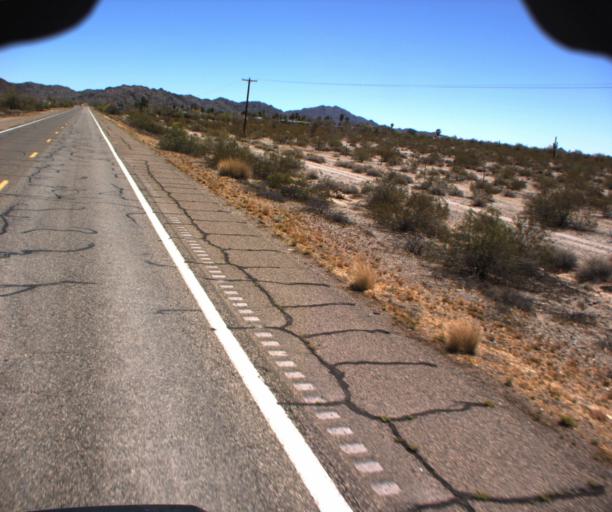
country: US
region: Arizona
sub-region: La Paz County
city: Salome
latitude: 33.7227
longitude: -113.7121
